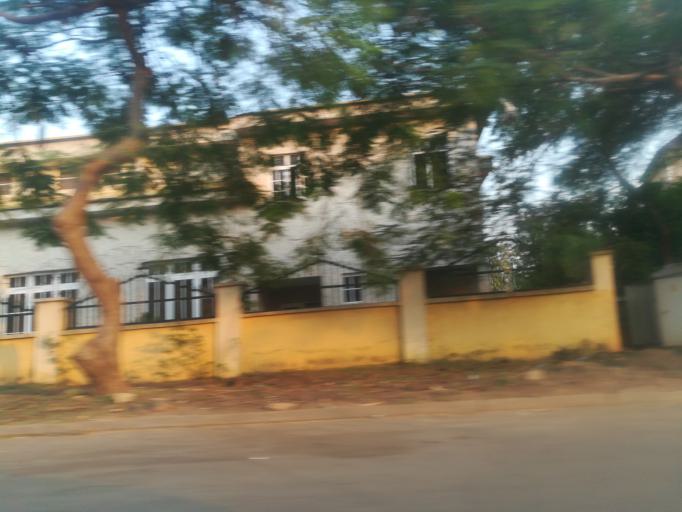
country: NG
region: Abuja Federal Capital Territory
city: Abuja
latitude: 9.0627
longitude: 7.4418
